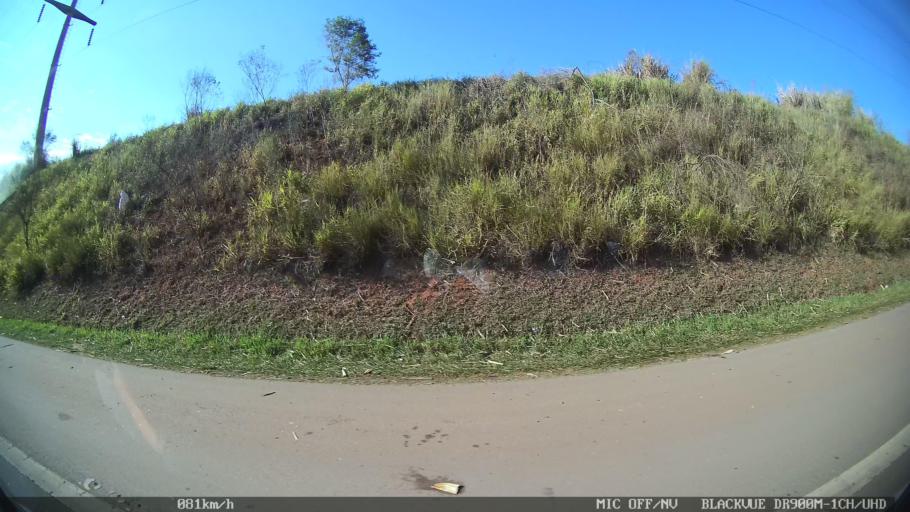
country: BR
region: Sao Paulo
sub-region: Piracicaba
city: Piracicaba
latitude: -22.6789
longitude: -47.5960
